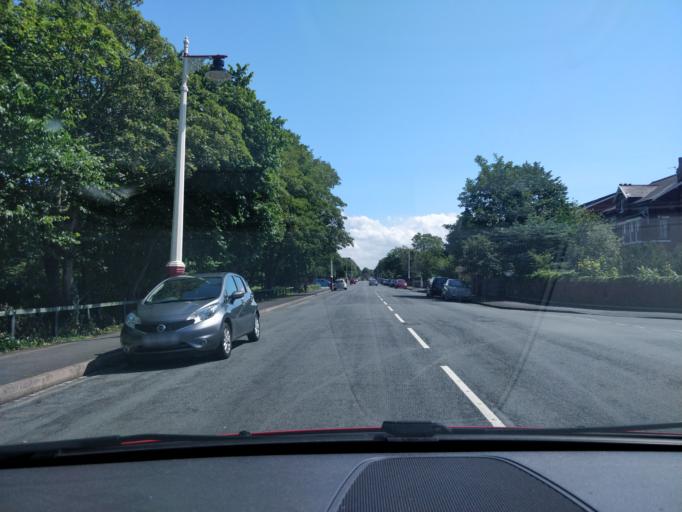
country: GB
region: England
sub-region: Sefton
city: Southport
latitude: 53.6578
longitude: -2.9946
